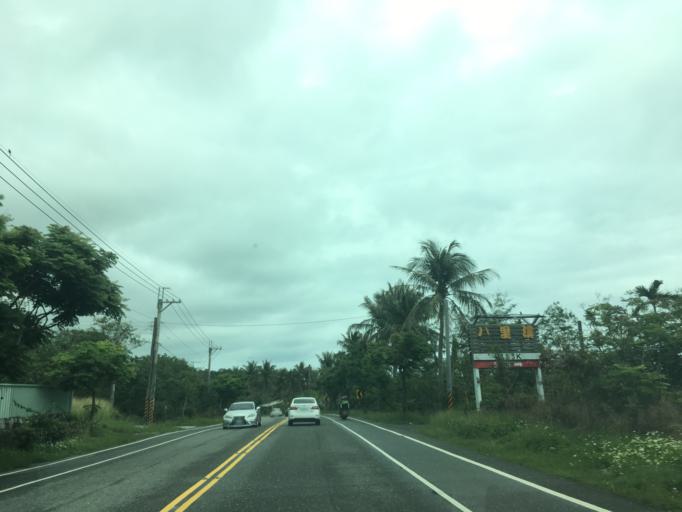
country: TW
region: Taiwan
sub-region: Taitung
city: Taitung
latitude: 22.8850
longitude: 121.2368
